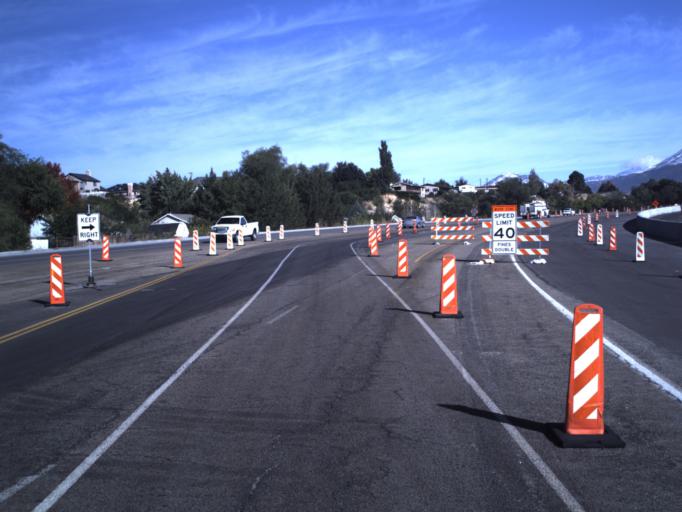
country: US
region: Utah
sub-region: Utah County
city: Provo
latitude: 40.2670
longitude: -111.6722
